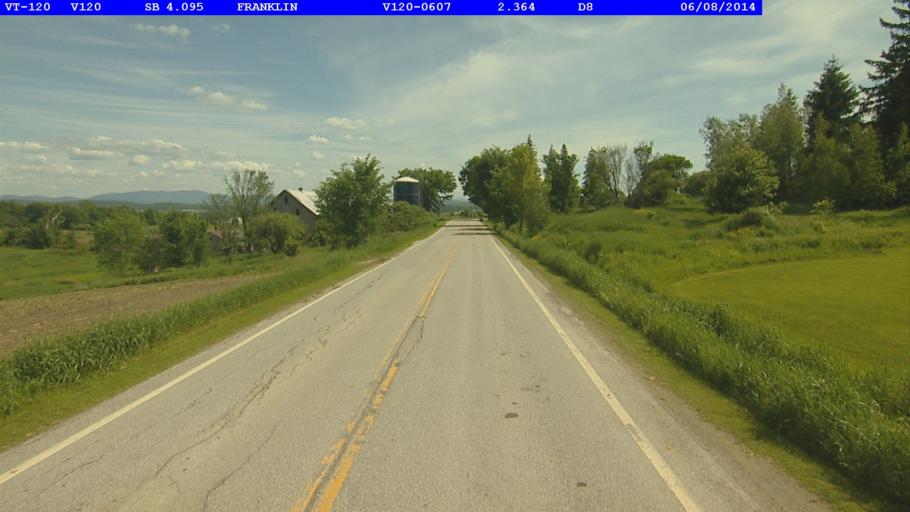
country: US
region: Vermont
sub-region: Franklin County
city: Enosburg Falls
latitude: 44.9670
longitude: -72.9081
